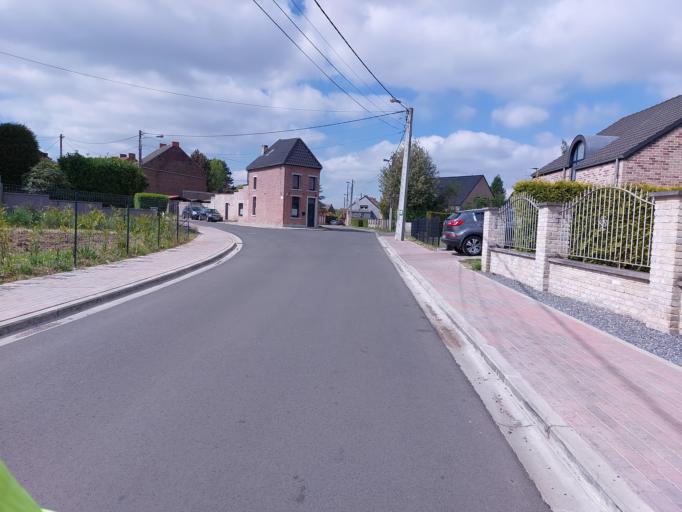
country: BE
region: Wallonia
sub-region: Province du Hainaut
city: Colfontaine
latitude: 50.4198
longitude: 3.8683
